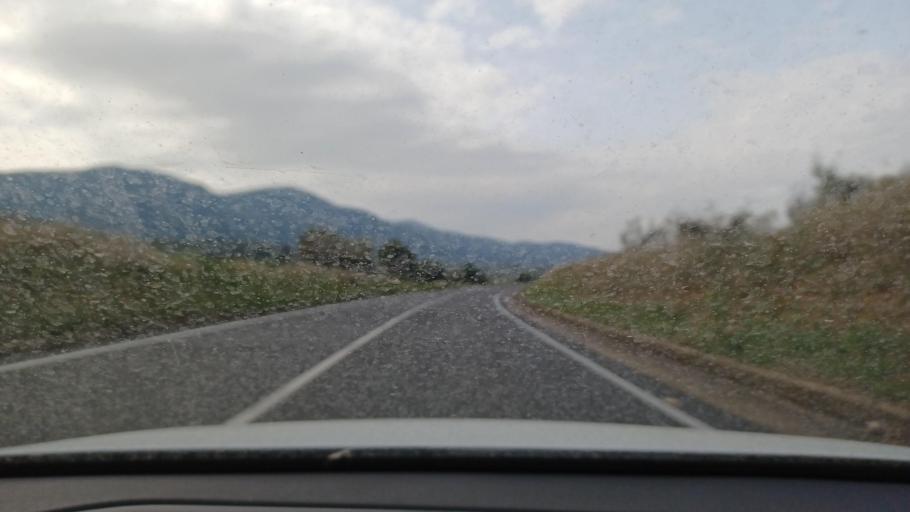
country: ES
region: Catalonia
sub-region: Provincia de Tarragona
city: Masdenverge
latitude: 40.6744
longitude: 0.5266
